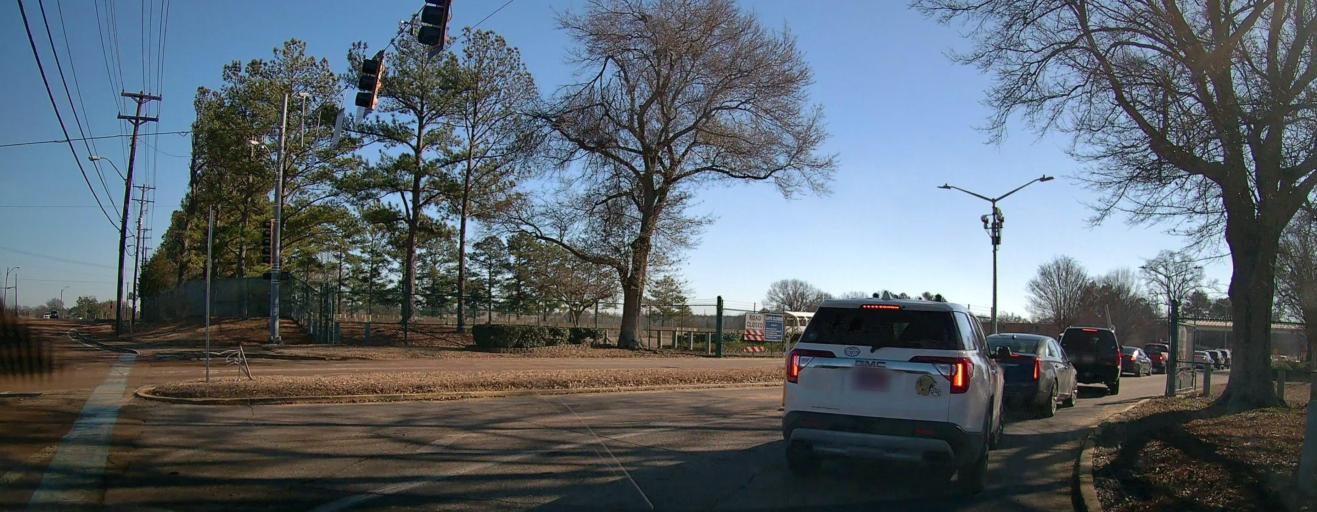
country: US
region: Tennessee
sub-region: Shelby County
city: Millington
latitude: 35.3402
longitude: -89.8778
